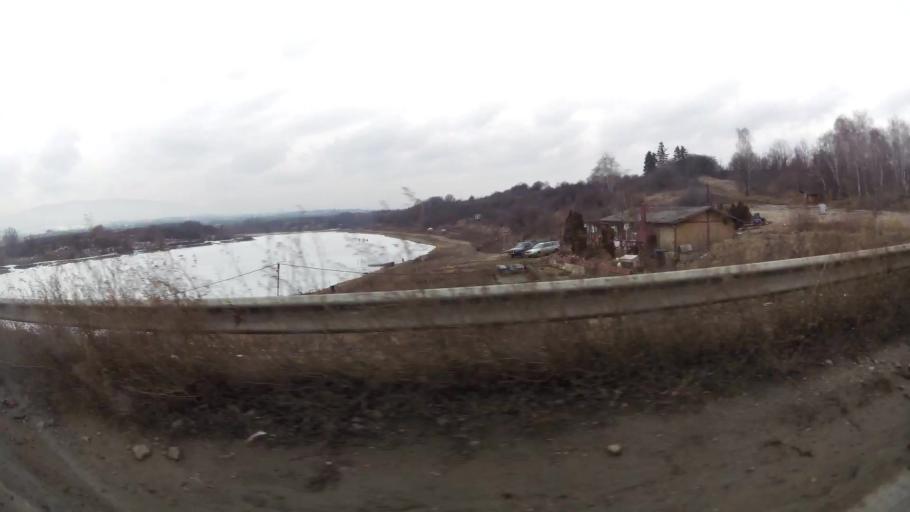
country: BG
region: Sofiya
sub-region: Obshtina Bozhurishte
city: Bozhurishte
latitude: 42.7086
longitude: 23.2303
